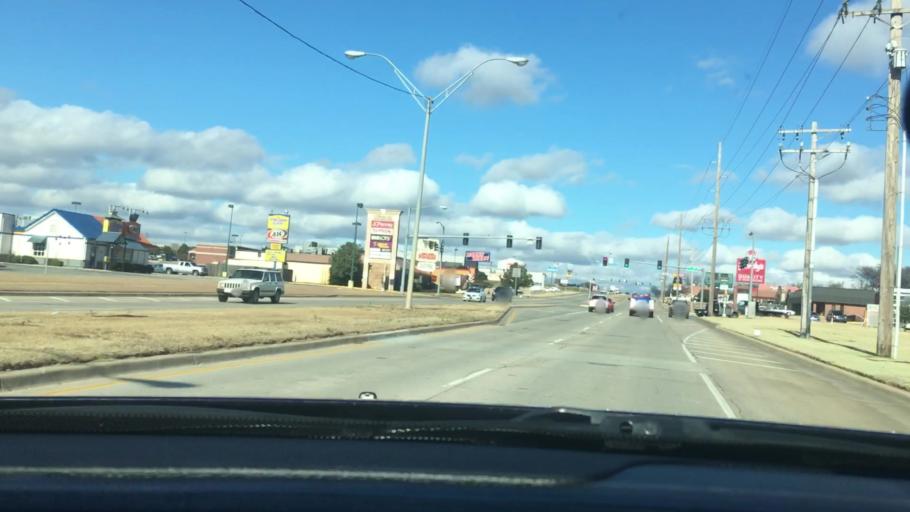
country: US
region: Oklahoma
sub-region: Carter County
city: Ardmore
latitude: 34.1888
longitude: -97.1429
